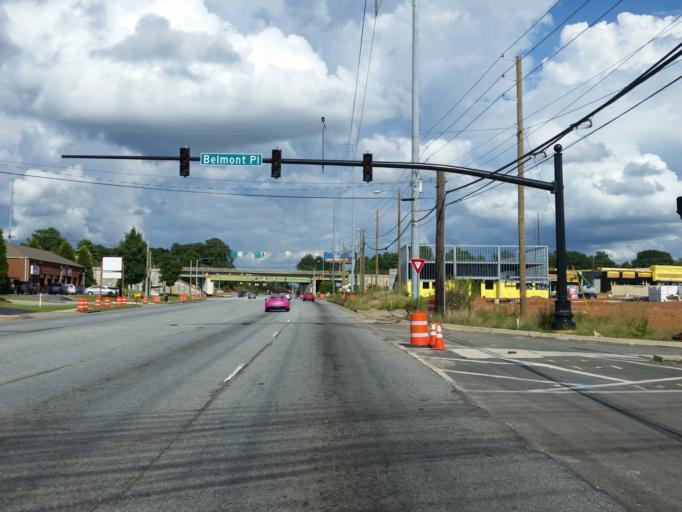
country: US
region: Georgia
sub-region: Cobb County
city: Smyrna
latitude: 33.8943
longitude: -84.5228
